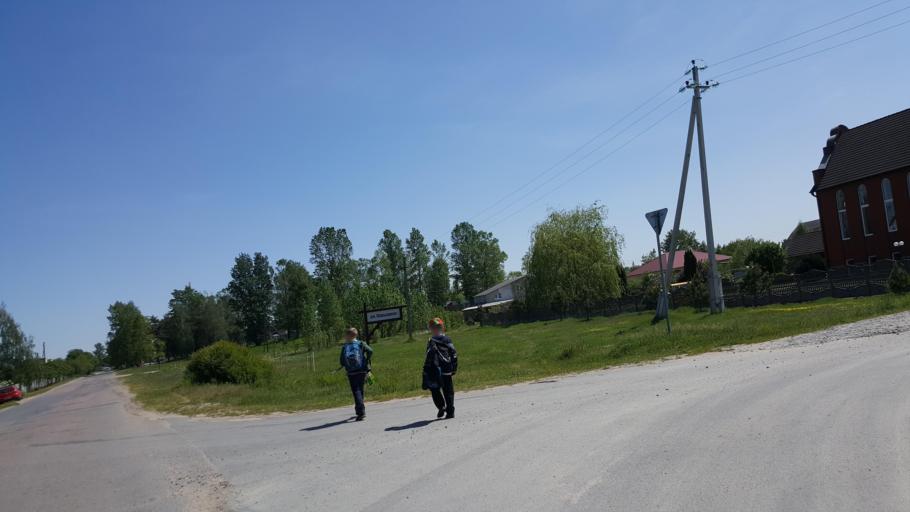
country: BY
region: Brest
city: Charnawchytsy
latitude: 52.2121
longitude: 23.7496
